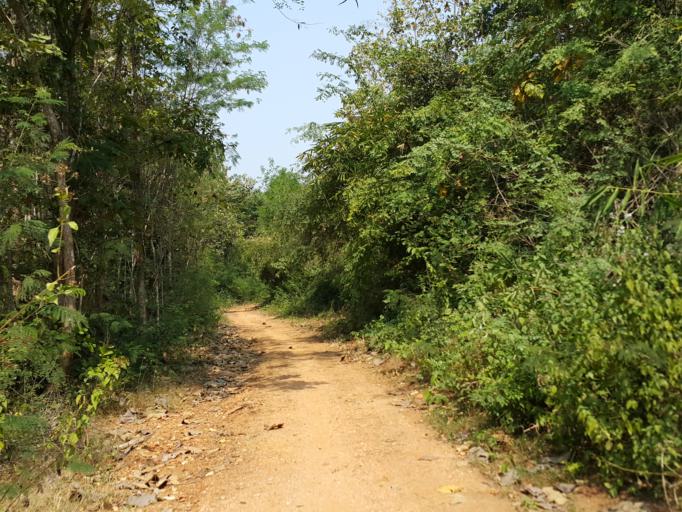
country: TH
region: Sukhothai
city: Thung Saliam
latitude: 17.3040
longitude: 99.5037
